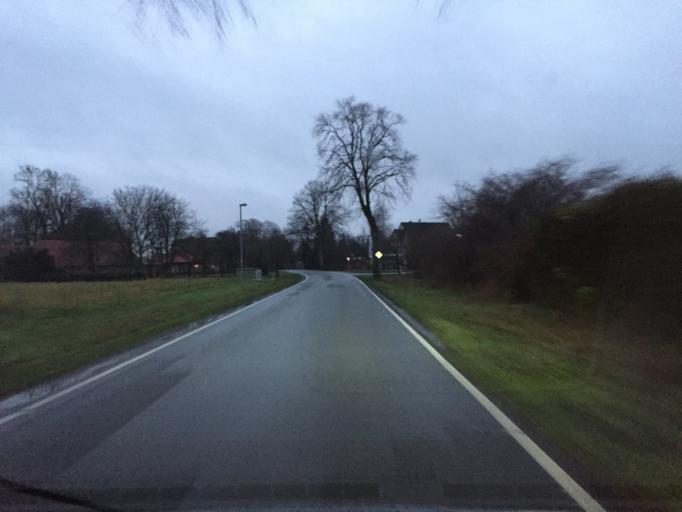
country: DE
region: Lower Saxony
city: Sudwalde
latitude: 52.7895
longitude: 8.8341
